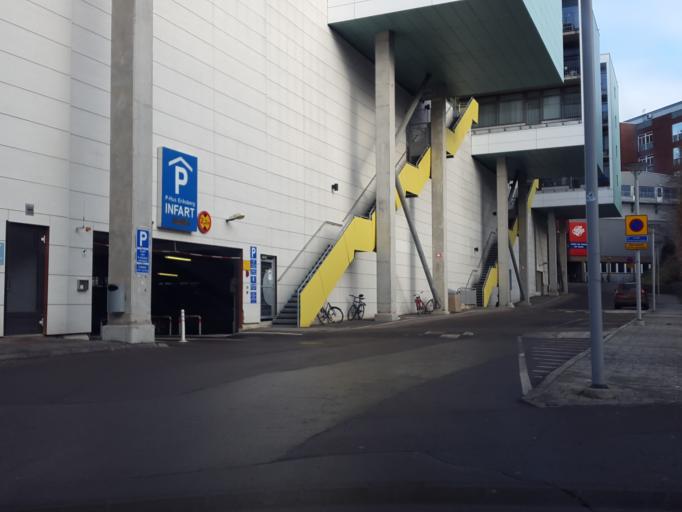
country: SE
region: Vaestra Goetaland
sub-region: Goteborg
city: Majorna
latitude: 57.7021
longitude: 11.9171
